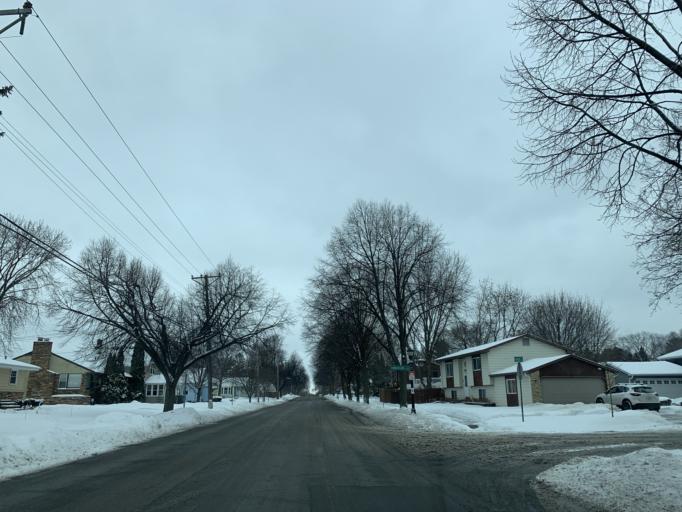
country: US
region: Minnesota
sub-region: Ramsey County
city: Roseville
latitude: 44.9846
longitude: -93.1171
